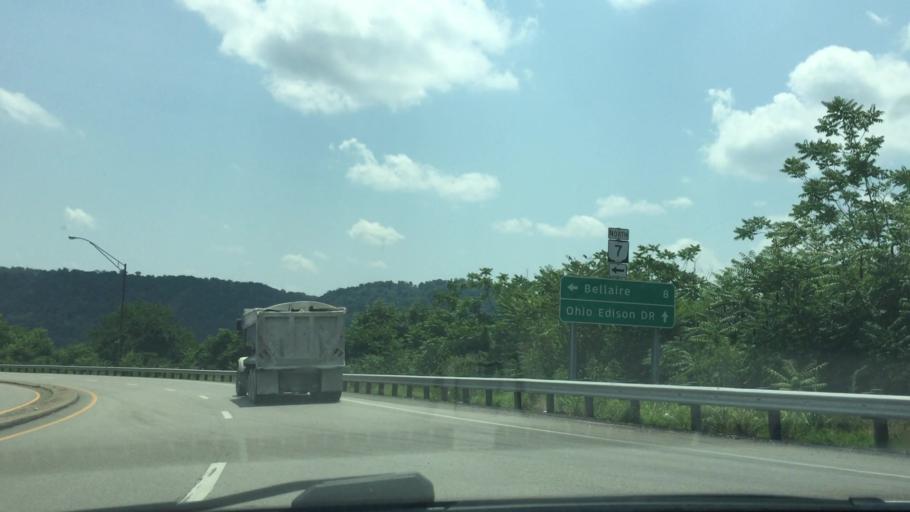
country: US
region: West Virginia
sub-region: Marshall County
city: Moundsville
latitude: 39.9149
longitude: -80.7621
